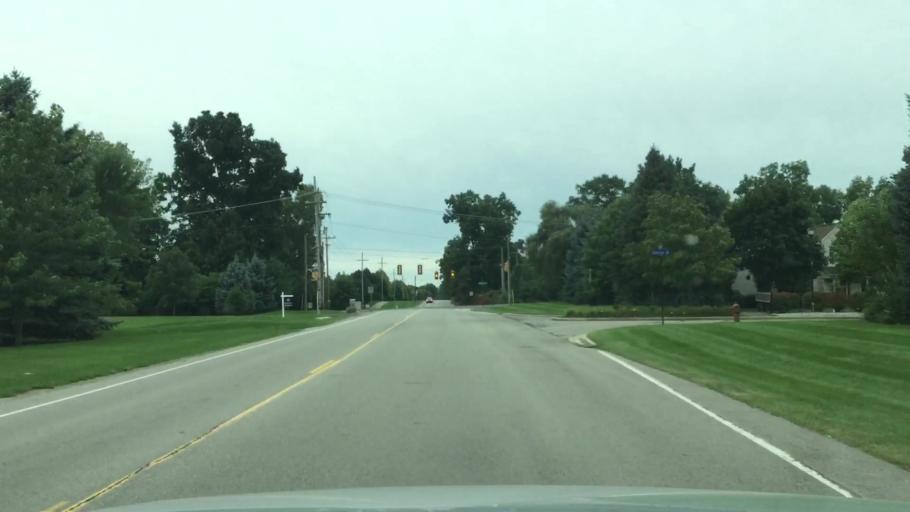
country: US
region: Michigan
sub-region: Washtenaw County
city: Ypsilanti
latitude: 42.2027
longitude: -83.6599
